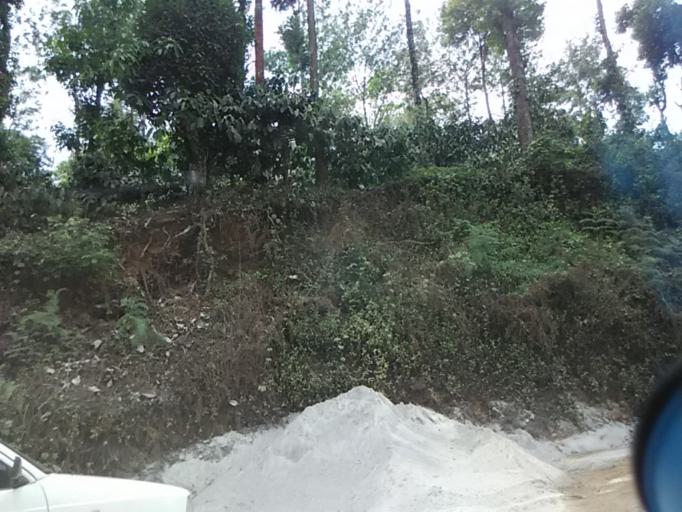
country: IN
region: Karnataka
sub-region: Kodagu
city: Virarajendrapet
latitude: 12.2073
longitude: 75.6734
